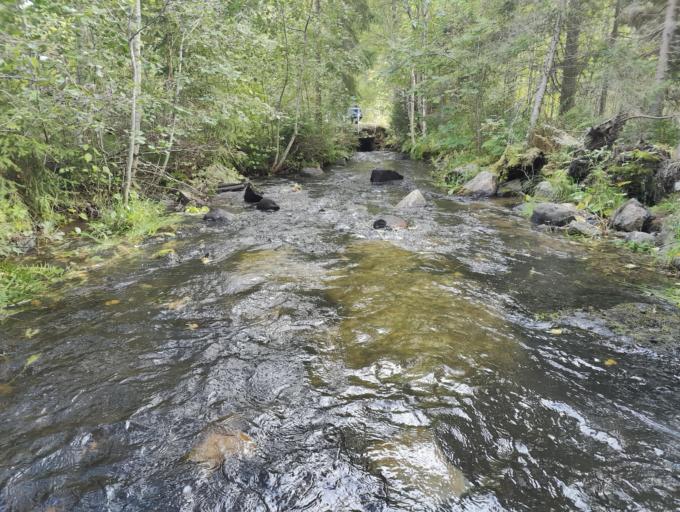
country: FI
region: Northern Savo
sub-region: Varkaus
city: Leppaevirta
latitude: 62.4897
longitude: 27.6956
